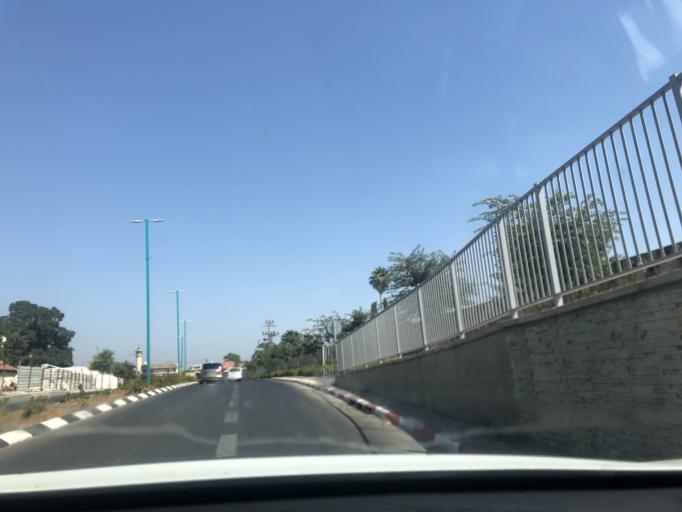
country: IL
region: Central District
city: Lod
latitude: 31.9575
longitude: 34.8941
